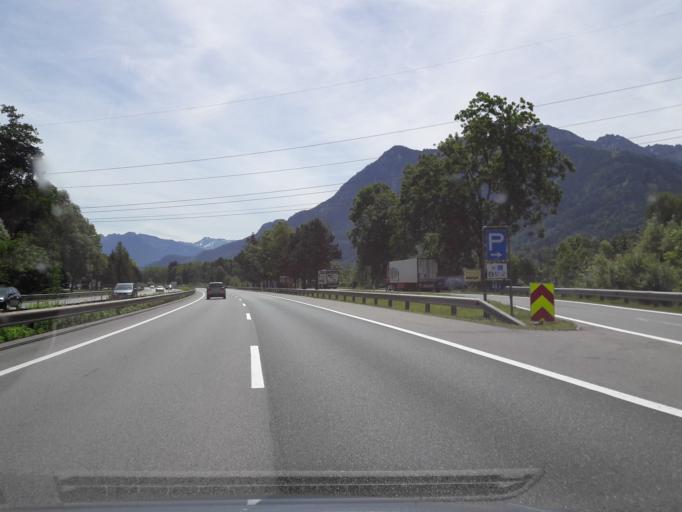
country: AT
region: Vorarlberg
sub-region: Politischer Bezirk Feldkirch
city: Satteins
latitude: 47.2026
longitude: 9.6753
